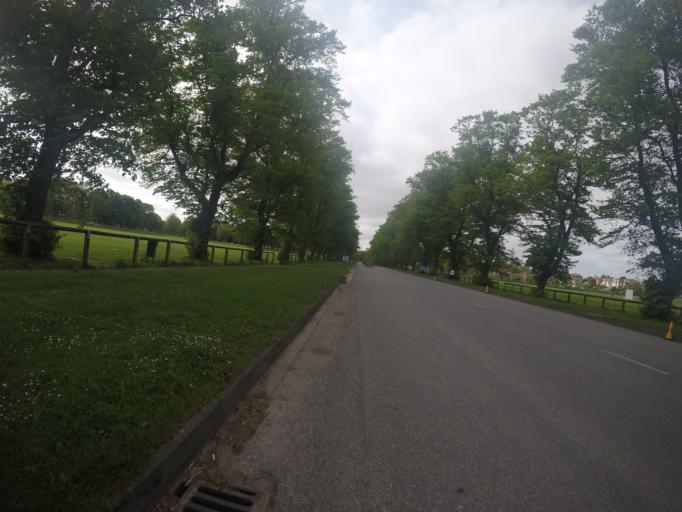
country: GB
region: England
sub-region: City of York
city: York
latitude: 53.9467
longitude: -1.0970
